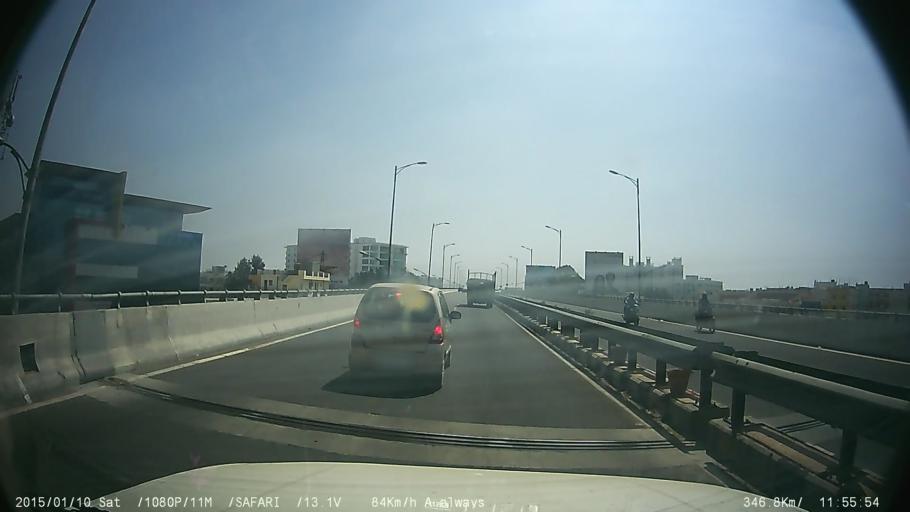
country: IN
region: Karnataka
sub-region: Bangalore Urban
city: Bangalore
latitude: 12.8689
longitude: 77.6542
